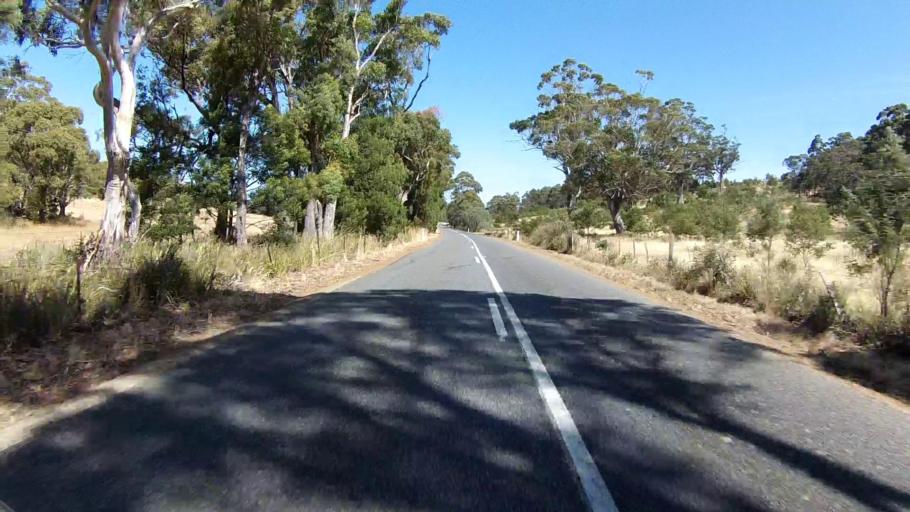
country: AU
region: Tasmania
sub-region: Sorell
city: Sorell
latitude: -42.3109
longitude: 147.9616
